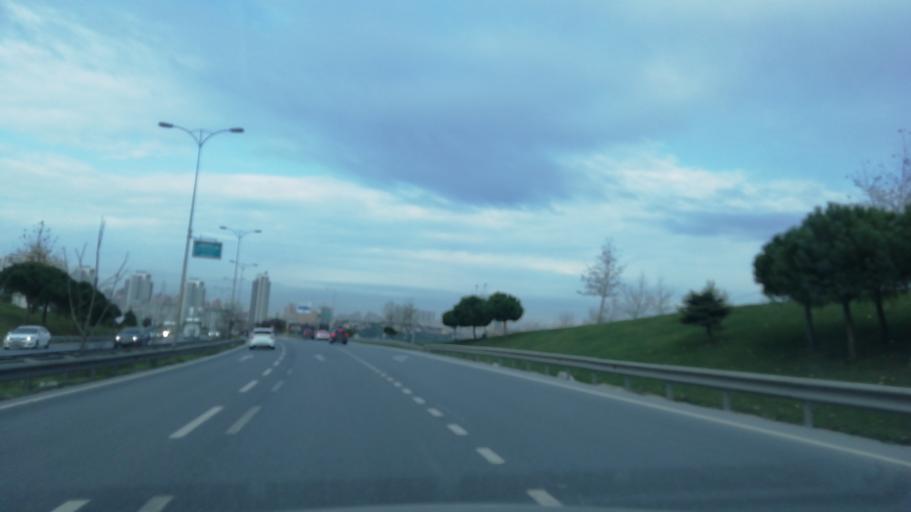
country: TR
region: Istanbul
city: Esenyurt
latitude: 41.0444
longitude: 28.6909
